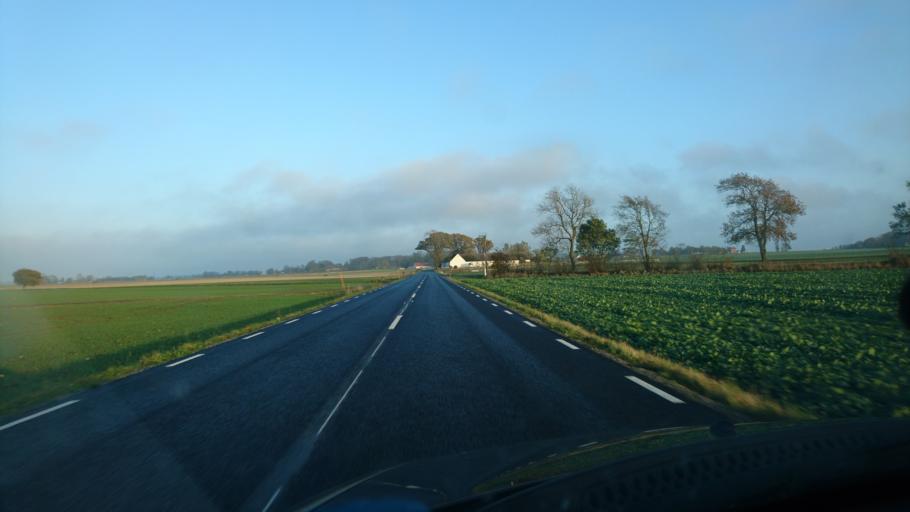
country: SE
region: Skane
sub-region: Tomelilla Kommun
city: Tomelilla
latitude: 55.4909
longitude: 14.0815
